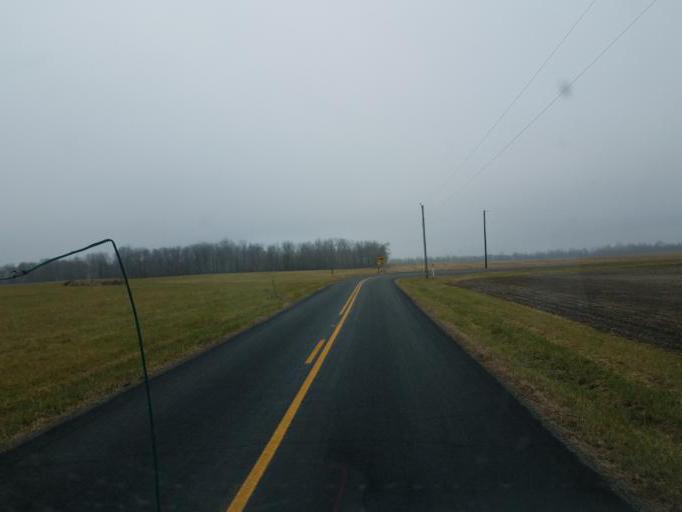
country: US
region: Ohio
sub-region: Champaign County
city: North Lewisburg
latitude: 40.2407
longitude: -83.5472
